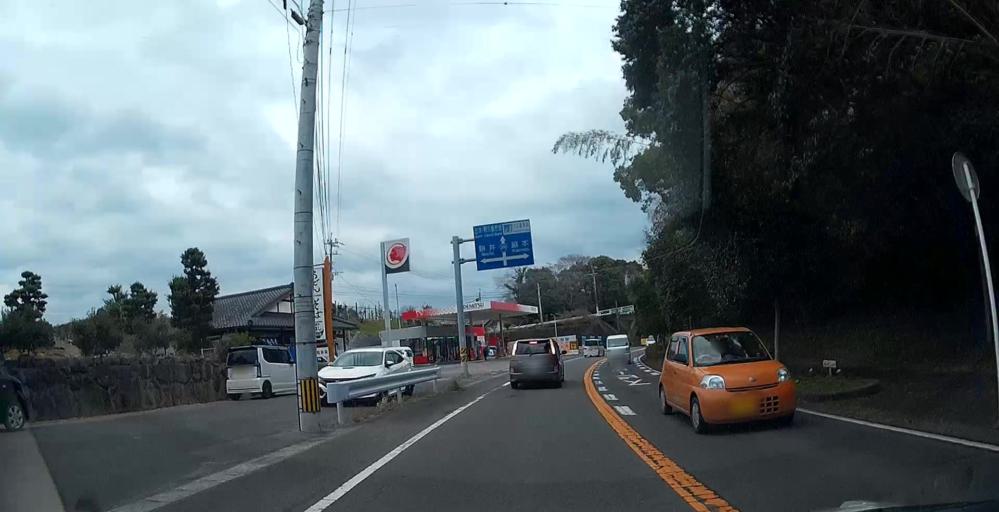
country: JP
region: Kagoshima
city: Akune
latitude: 32.0804
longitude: 130.2044
